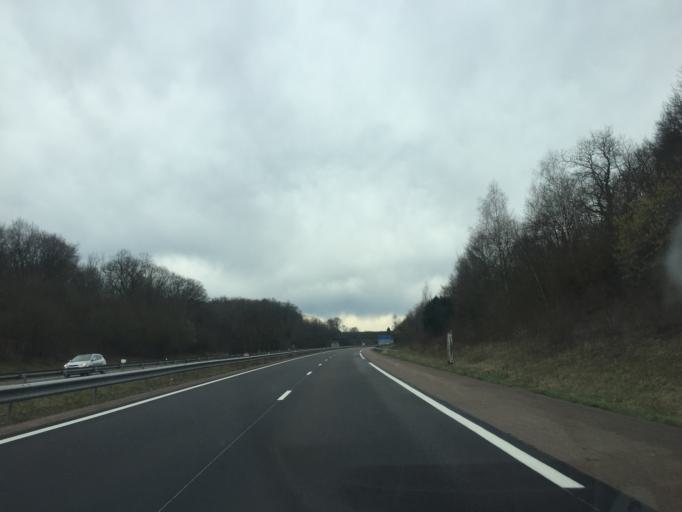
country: FR
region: Franche-Comte
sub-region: Departement du Jura
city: Bletterans
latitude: 46.7854
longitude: 5.5277
